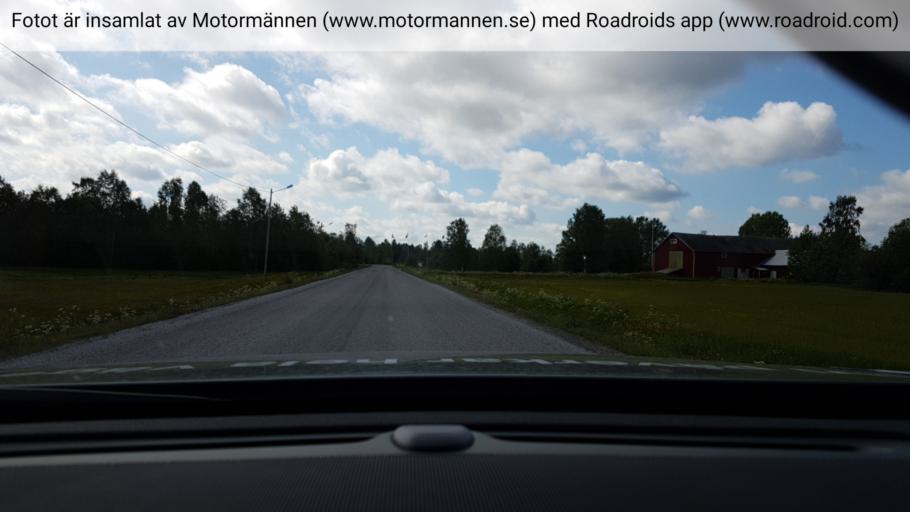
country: SE
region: Vaesterbotten
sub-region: Vannas Kommun
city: Vannasby
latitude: 63.9261
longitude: 19.8553
